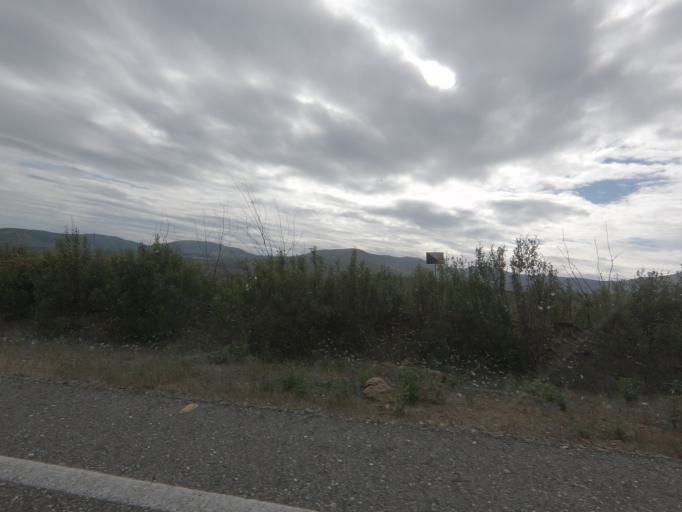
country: ES
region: Extremadura
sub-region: Provincia de Caceres
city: Acebo
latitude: 40.2087
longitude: -6.6763
